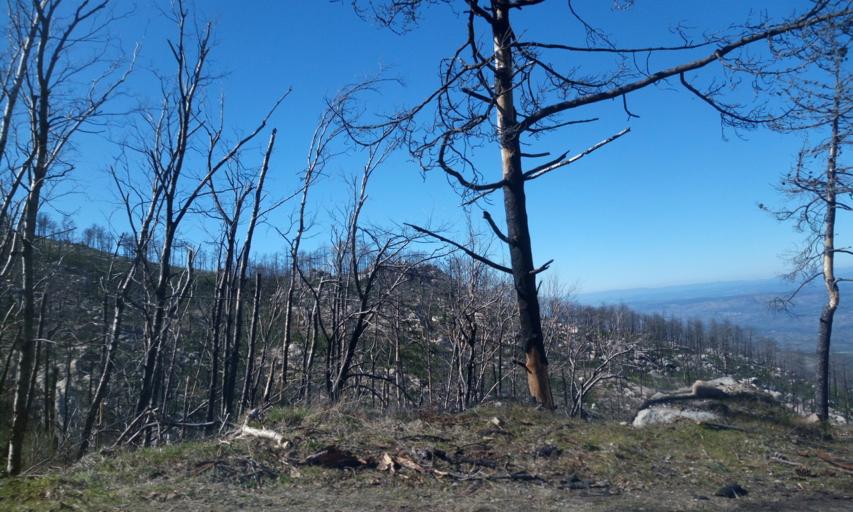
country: PT
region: Guarda
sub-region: Manteigas
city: Manteigas
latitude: 40.4884
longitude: -7.5231
